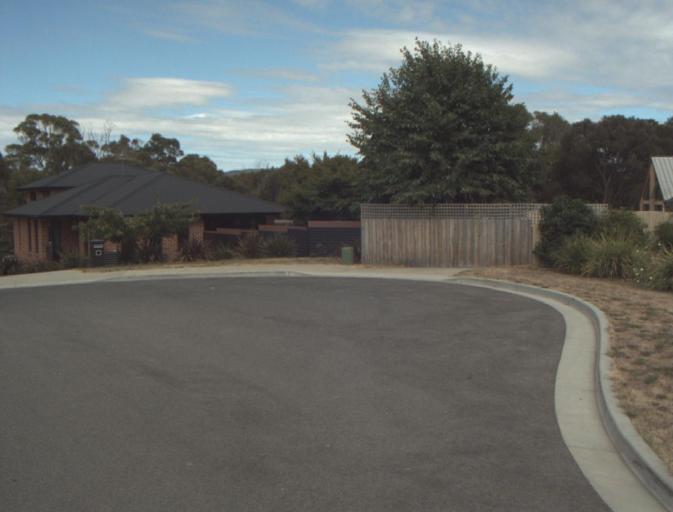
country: AU
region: Tasmania
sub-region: Launceston
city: West Launceston
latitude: -41.4575
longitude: 147.1223
